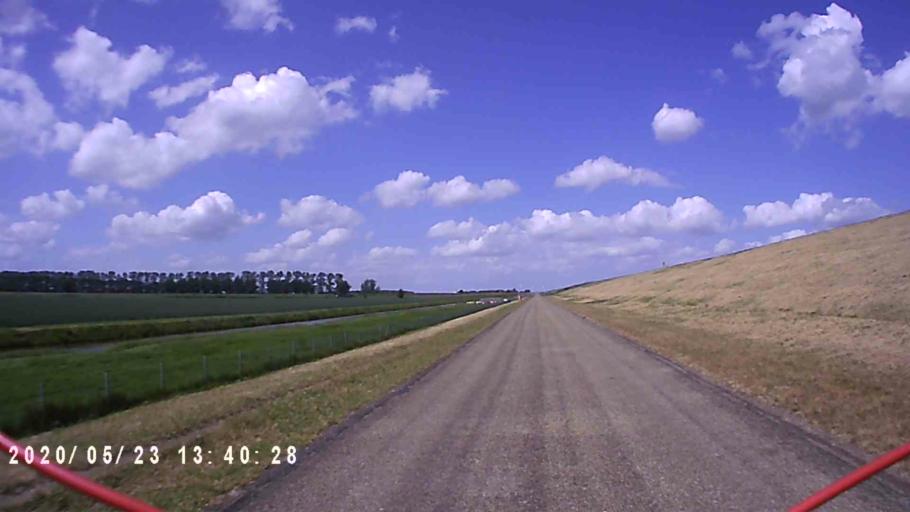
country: NL
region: Groningen
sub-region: Gemeente  Oldambt
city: Winschoten
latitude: 53.2632
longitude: 7.0723
